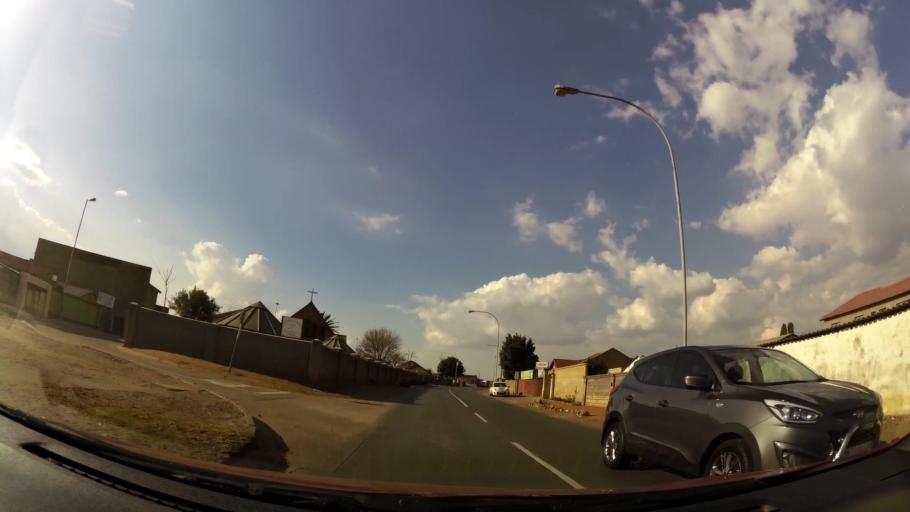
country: ZA
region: Gauteng
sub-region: City of Johannesburg Metropolitan Municipality
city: Soweto
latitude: -26.2320
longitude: 27.8664
